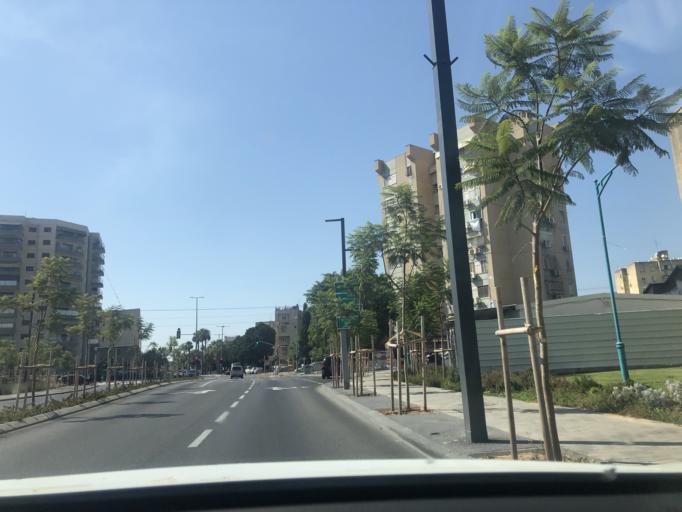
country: IL
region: Central District
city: Lod
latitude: 31.9443
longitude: 34.8950
